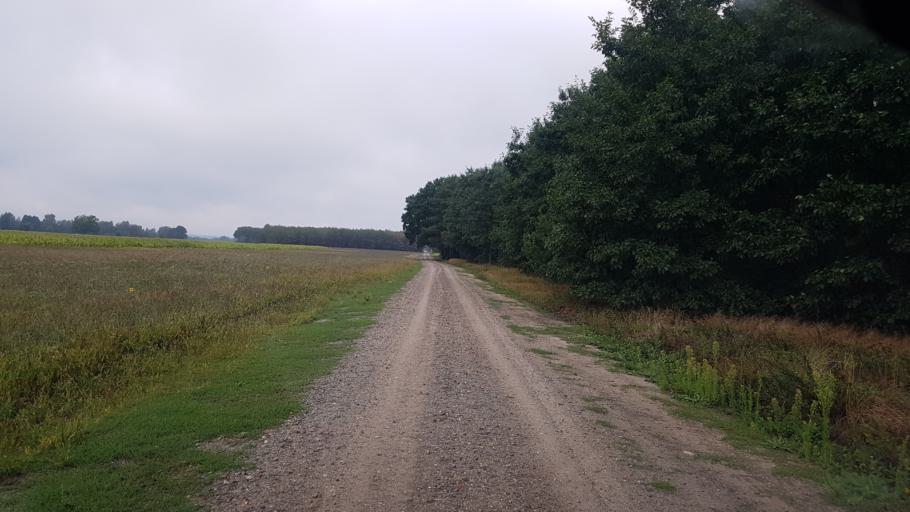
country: DE
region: Brandenburg
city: Ruckersdorf
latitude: 51.5576
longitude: 13.5666
